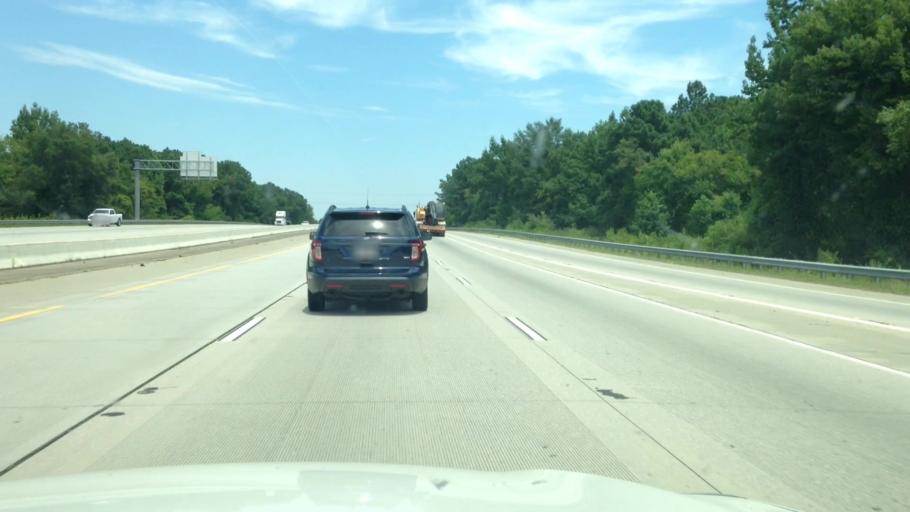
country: US
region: South Carolina
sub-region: Florence County
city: Florence
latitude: 34.2324
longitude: -79.7944
